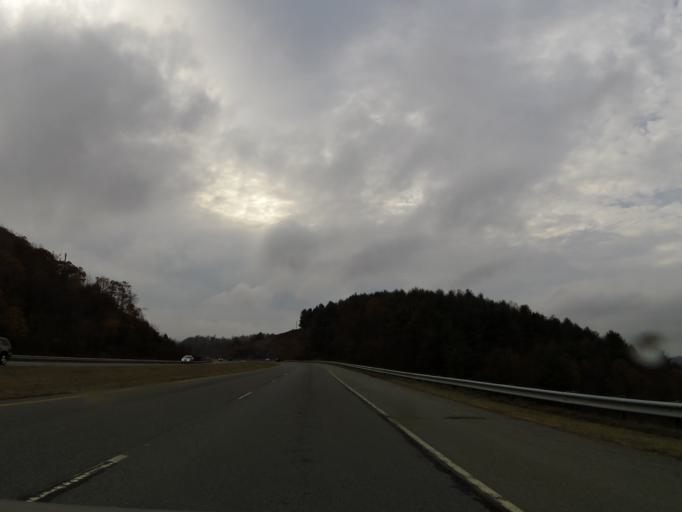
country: US
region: North Carolina
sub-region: Watauga County
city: Boone
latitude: 36.2345
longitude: -81.5699
